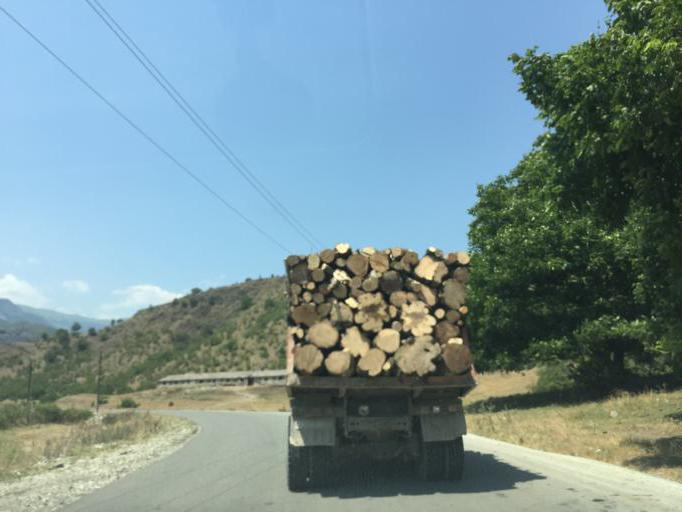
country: AZ
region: Kalbacar Rayonu
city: Kerbakhiar
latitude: 40.1365
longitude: 46.3660
